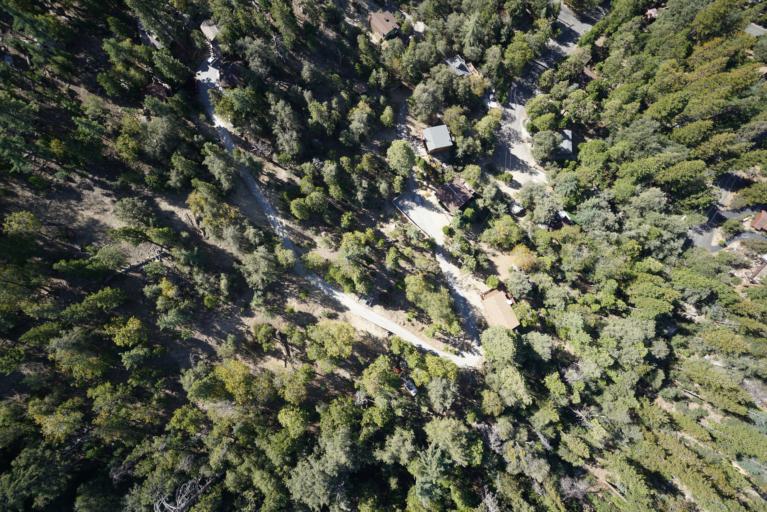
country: US
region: California
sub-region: Riverside County
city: Idyllwild
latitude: 33.7489
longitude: -116.6950
